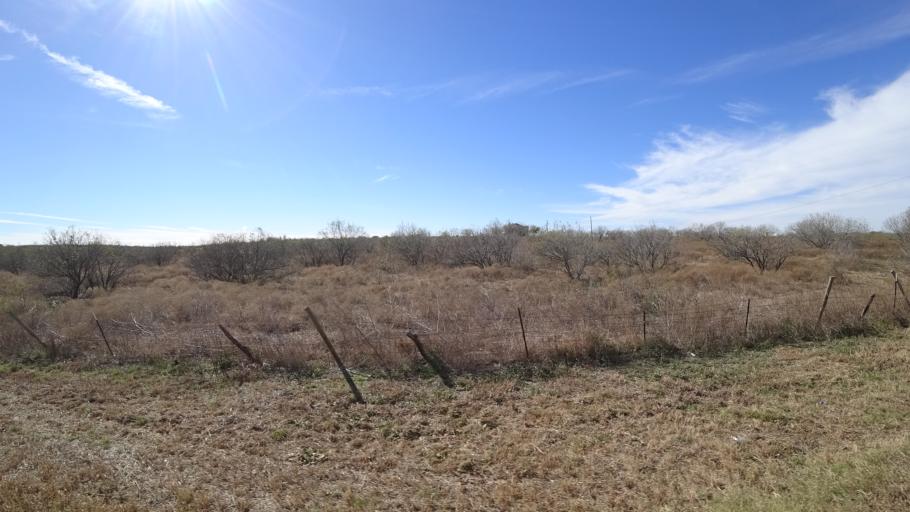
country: US
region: Texas
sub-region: Travis County
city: Onion Creek
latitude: 30.1024
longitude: -97.6879
